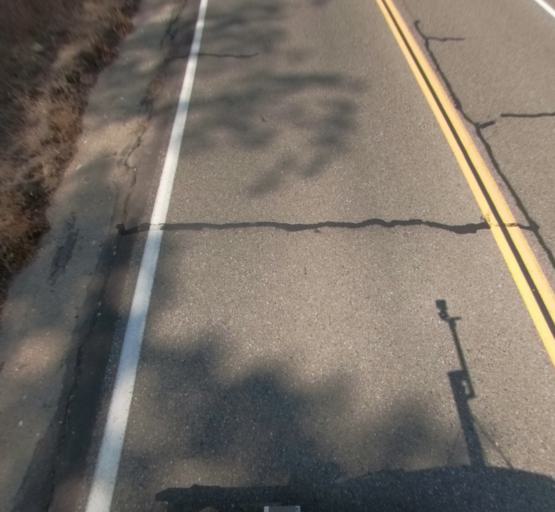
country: US
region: California
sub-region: Madera County
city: Yosemite Lakes
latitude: 37.2254
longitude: -119.7685
